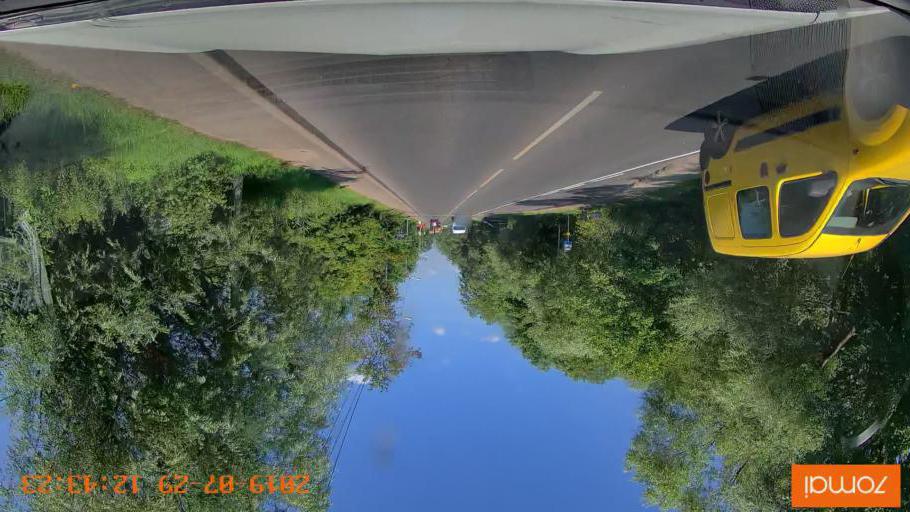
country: RU
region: Kaliningrad
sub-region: Gorod Kaliningrad
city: Kaliningrad
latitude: 54.6759
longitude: 20.5409
